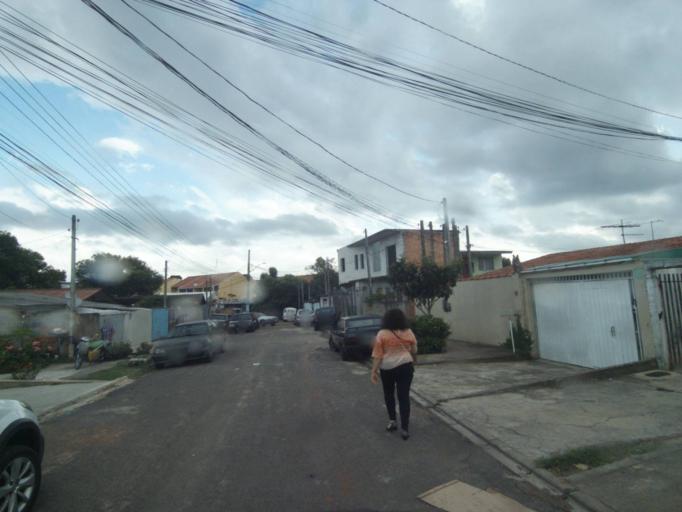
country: BR
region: Parana
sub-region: Pinhais
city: Pinhais
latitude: -25.4445
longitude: -49.2142
